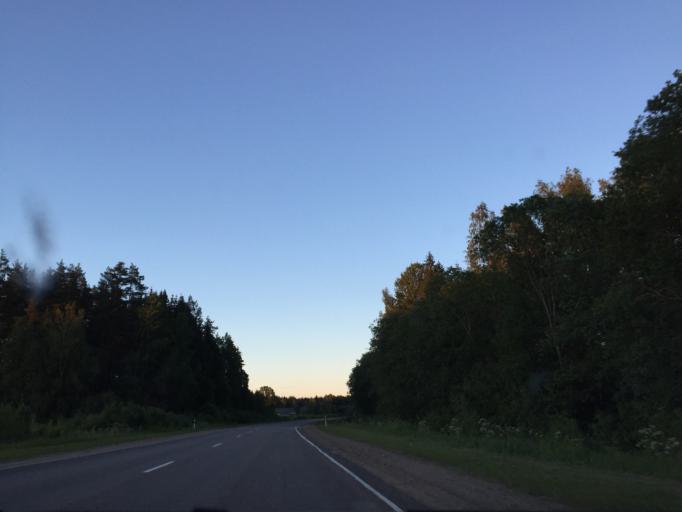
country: LV
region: Smiltene
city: Smiltene
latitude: 57.4407
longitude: 26.1858
